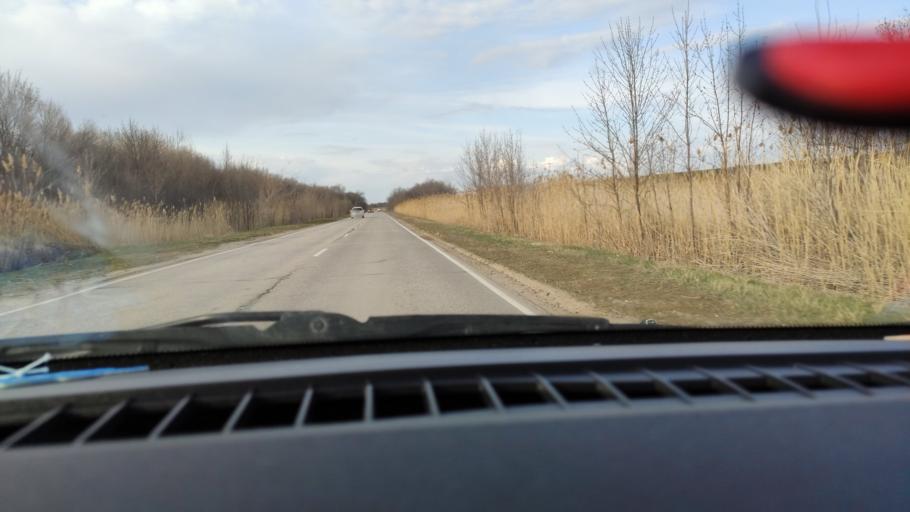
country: RU
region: Saratov
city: Privolzhskiy
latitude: 51.2599
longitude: 45.9449
